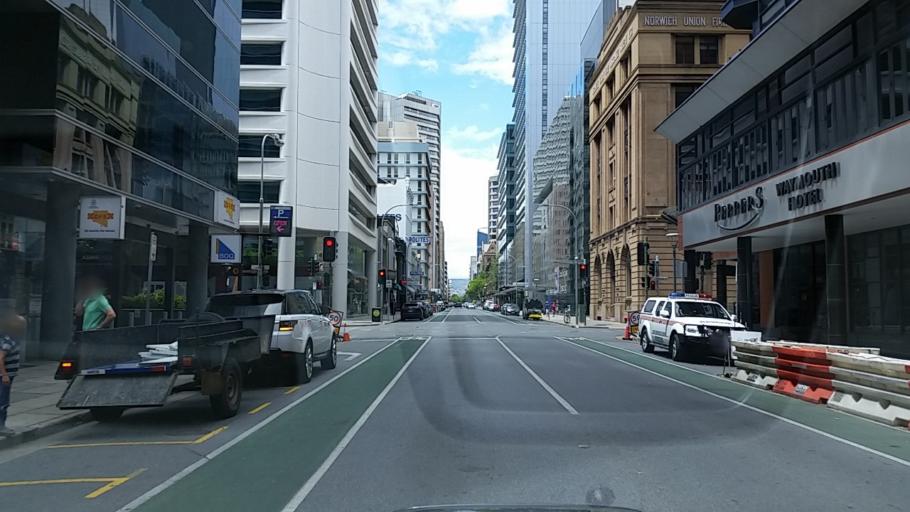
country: AU
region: South Australia
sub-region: Adelaide
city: Adelaide
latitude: -34.9259
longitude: 138.5972
